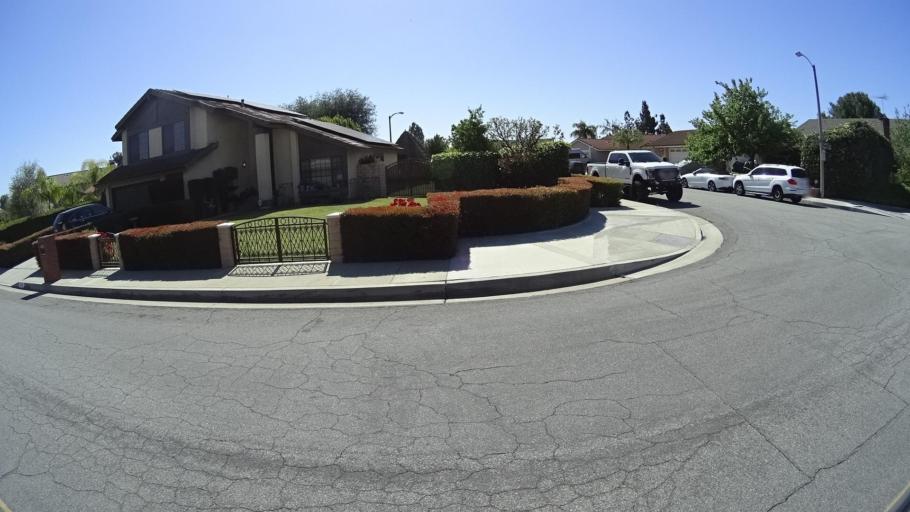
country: US
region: California
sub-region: Los Angeles County
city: Diamond Bar
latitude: 33.9987
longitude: -117.8268
